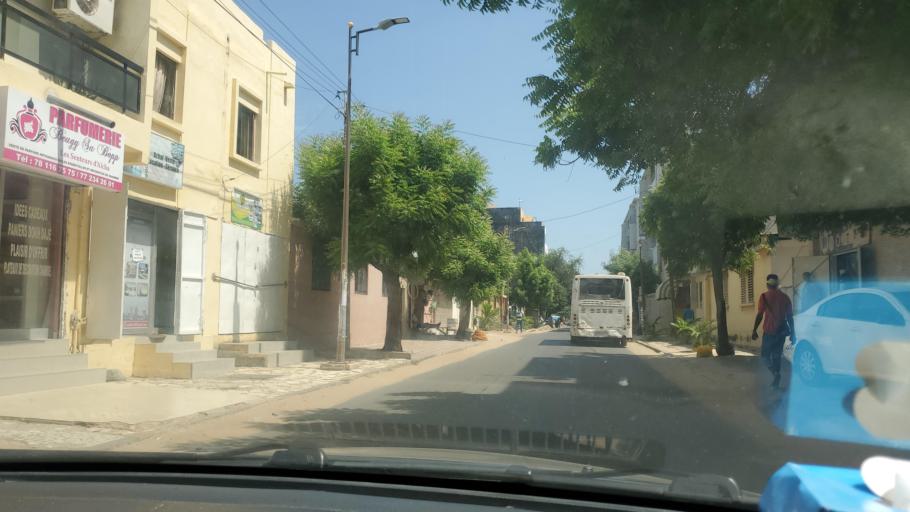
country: SN
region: Dakar
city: Grand Dakar
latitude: 14.7047
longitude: -17.4598
